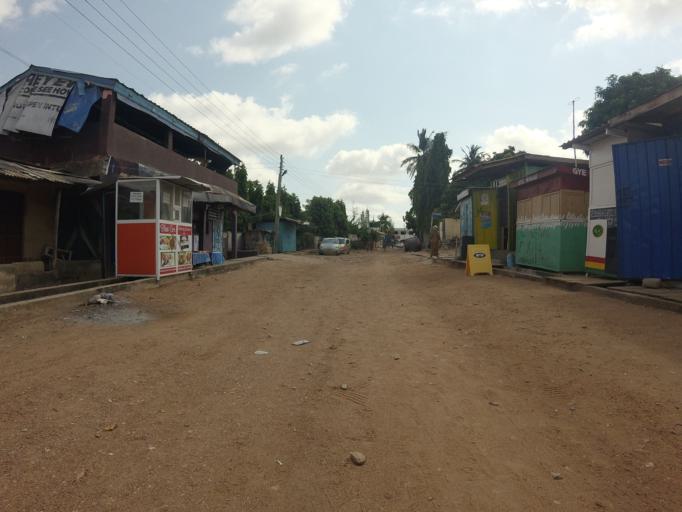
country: GH
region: Greater Accra
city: Dome
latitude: 5.6161
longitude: -0.2426
